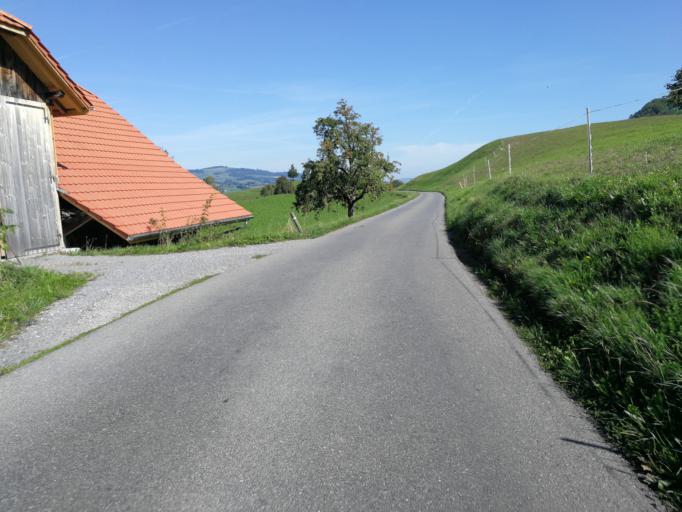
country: CH
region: Lucerne
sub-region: Lucerne-Land District
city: Weggis
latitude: 47.0418
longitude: 8.4269
